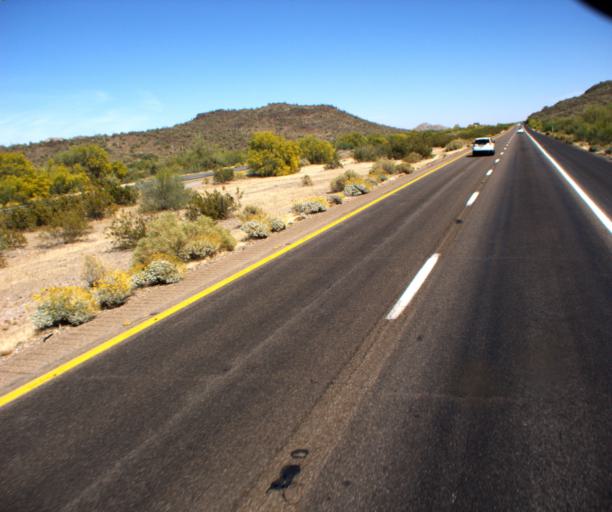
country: US
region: Arizona
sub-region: Pinal County
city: Maricopa
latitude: 32.8359
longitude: -112.1983
